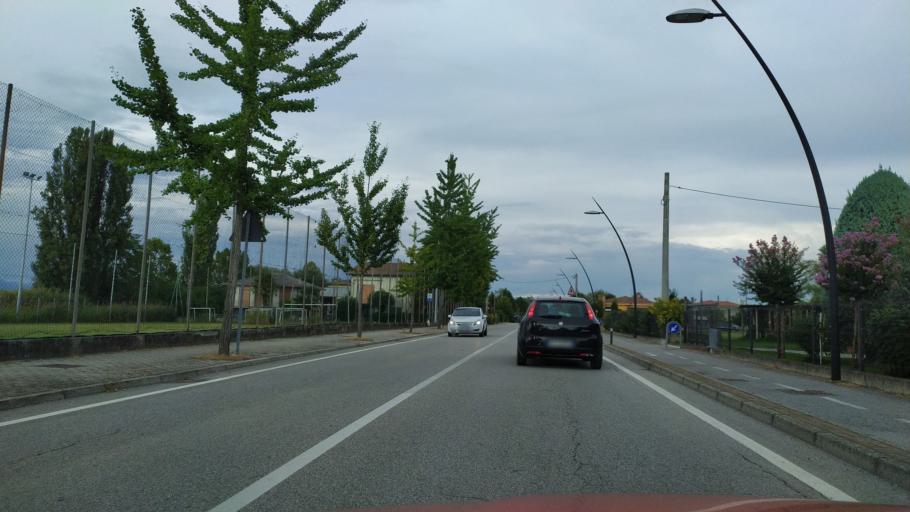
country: IT
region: Veneto
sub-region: Provincia di Padova
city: San Giorgio in Bosco
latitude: 45.5834
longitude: 11.7946
